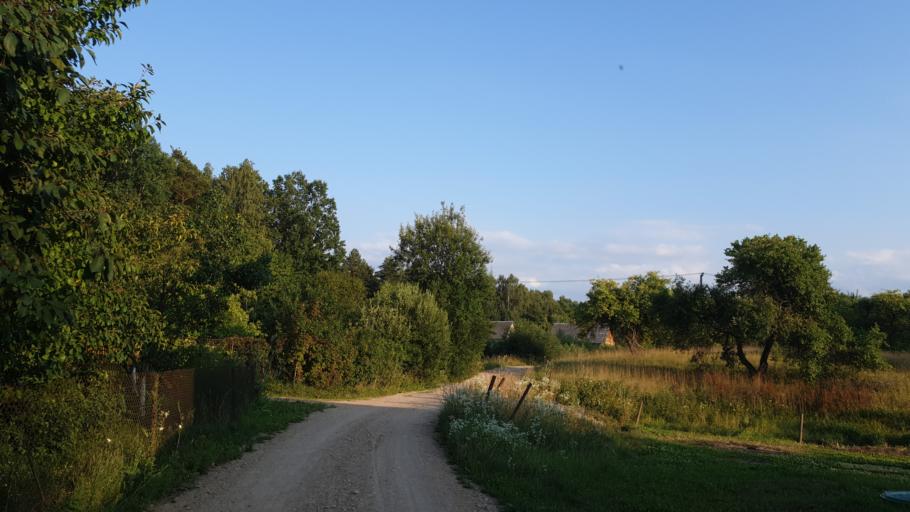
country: LT
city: Grigiskes
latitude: 54.7604
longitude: 25.0274
